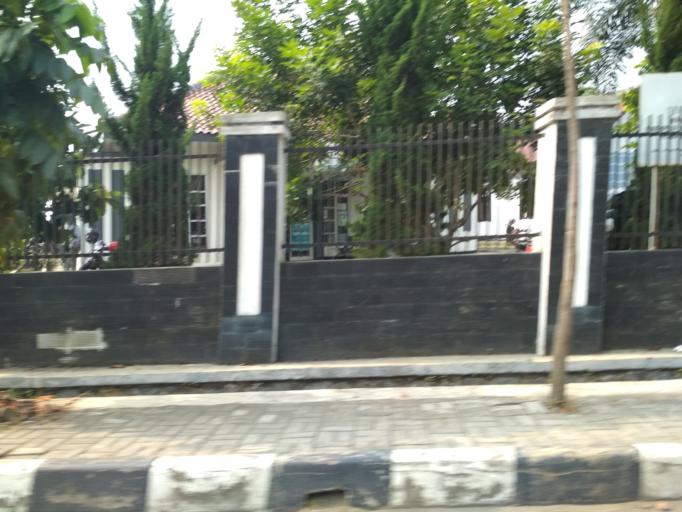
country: ID
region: West Java
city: Bogor
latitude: -6.5788
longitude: 106.7600
